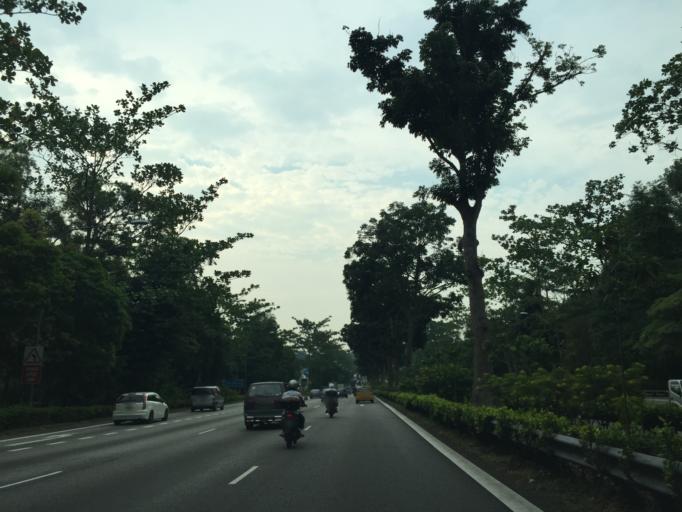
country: MY
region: Johor
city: Johor Bahru
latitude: 1.3859
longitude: 103.7750
